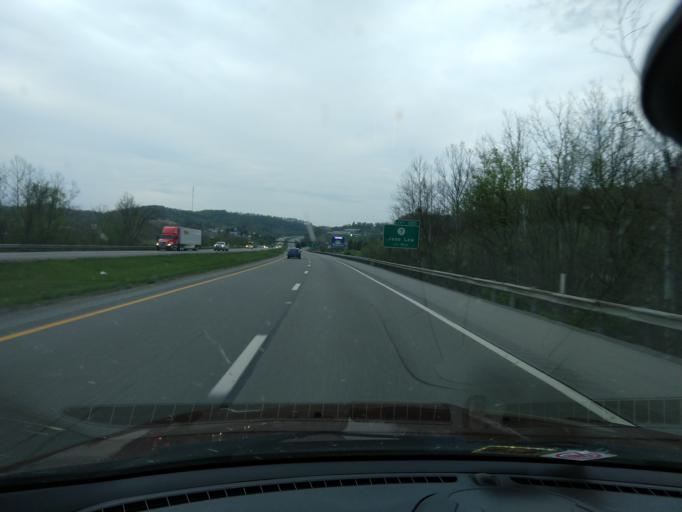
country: US
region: West Virginia
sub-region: Lewis County
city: Weston
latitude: 39.0961
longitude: -80.3921
